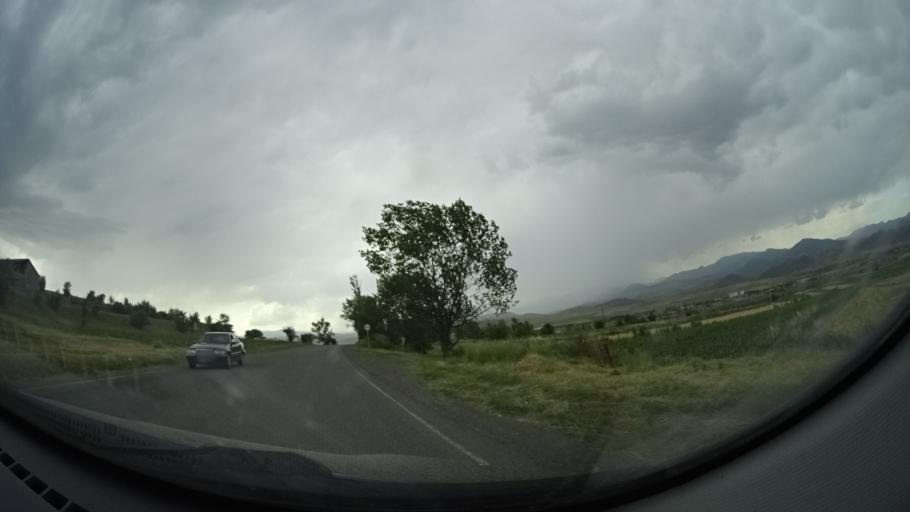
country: GE
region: Samtskhe-Javakheti
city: Akhaltsikhe
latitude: 41.6393
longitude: 43.0312
